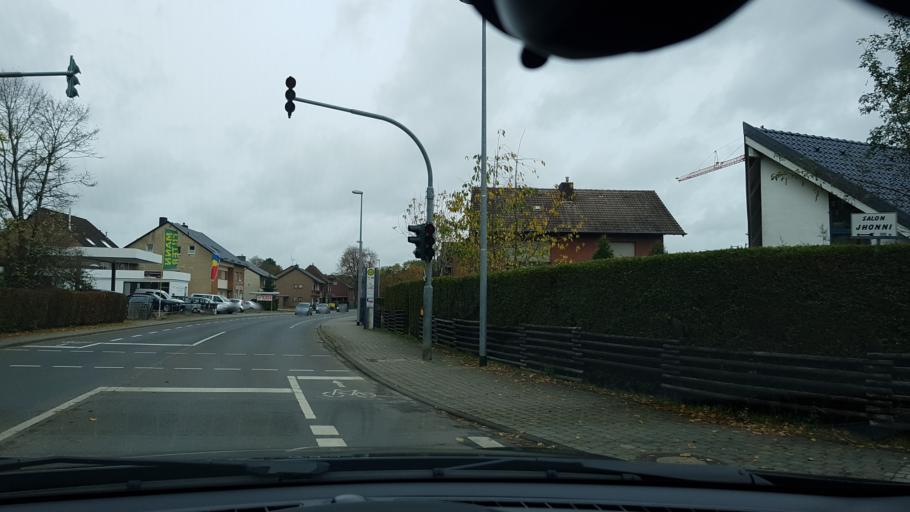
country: DE
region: North Rhine-Westphalia
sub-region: Regierungsbezirk Koln
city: Bedburg
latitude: 51.0051
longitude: 6.5592
